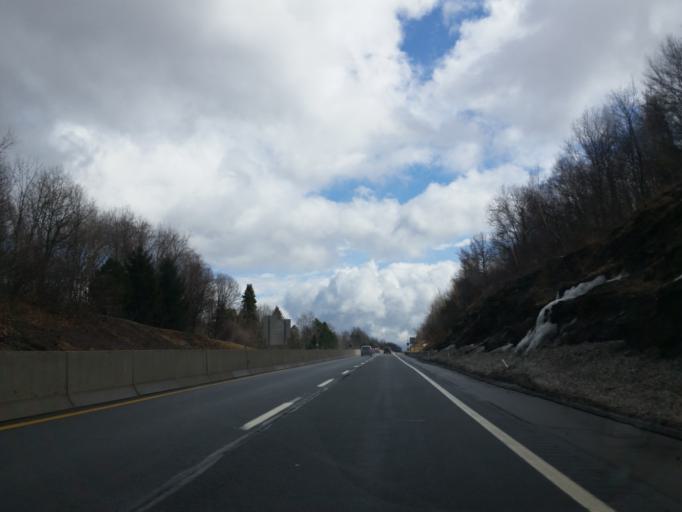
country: US
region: Pennsylvania
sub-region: Lackawanna County
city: Chinchilla
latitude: 41.4662
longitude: -75.6996
